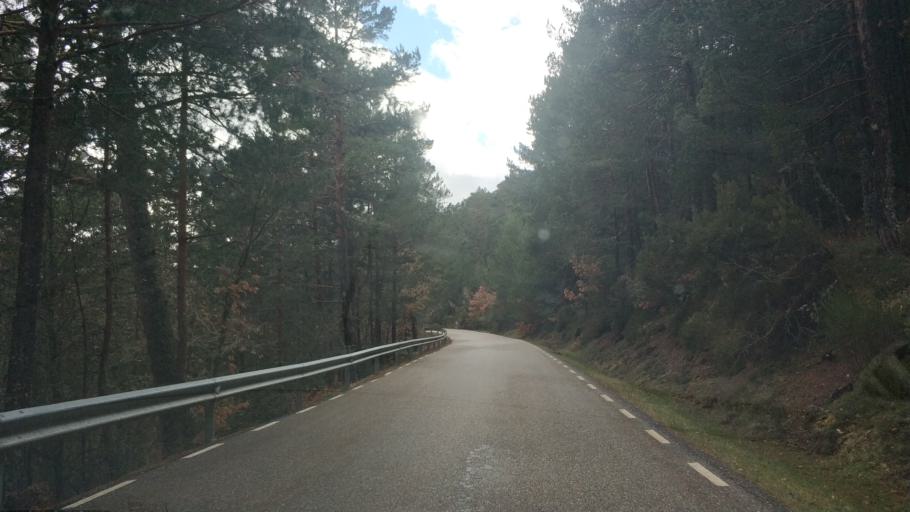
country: ES
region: Castille and Leon
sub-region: Provincia de Burgos
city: Quintanar de la Sierra
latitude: 42.0164
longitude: -3.0175
